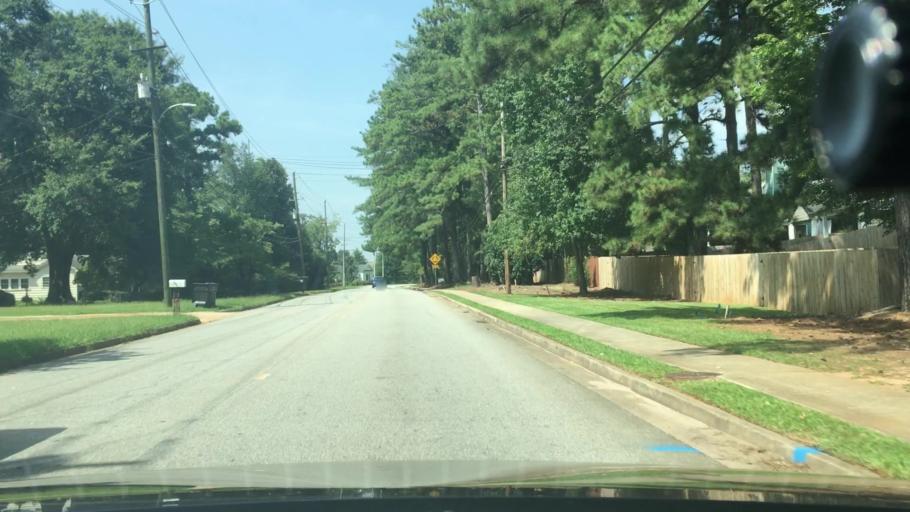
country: US
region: Georgia
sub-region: Coweta County
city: East Newnan
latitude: 33.3658
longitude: -84.7794
